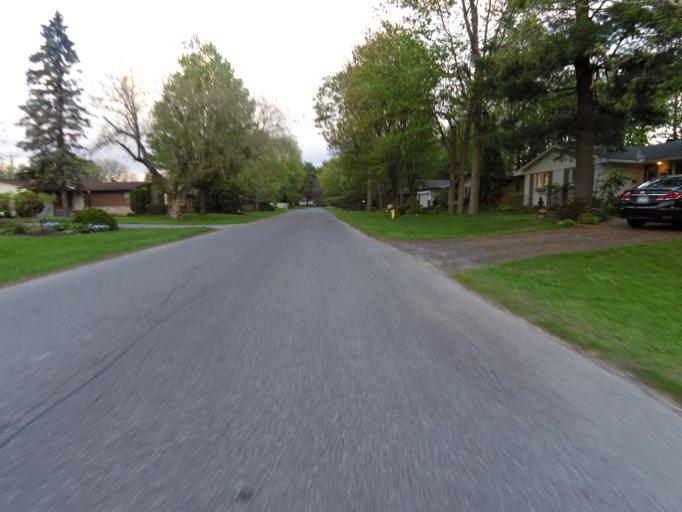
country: CA
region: Ontario
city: Bells Corners
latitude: 45.3226
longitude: -75.8200
